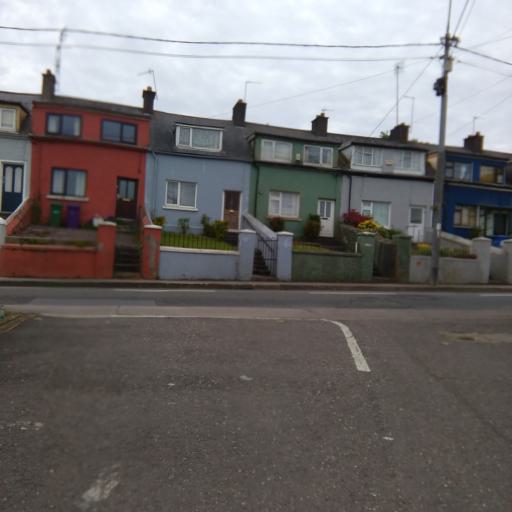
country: IE
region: Munster
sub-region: County Cork
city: Cork
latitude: 51.9102
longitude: -8.4543
